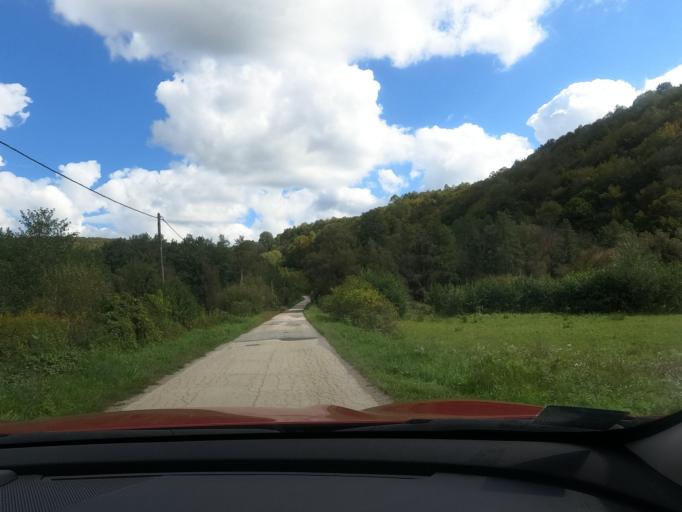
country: BA
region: Federation of Bosnia and Herzegovina
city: Velika Kladusa
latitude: 45.2370
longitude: 15.7508
